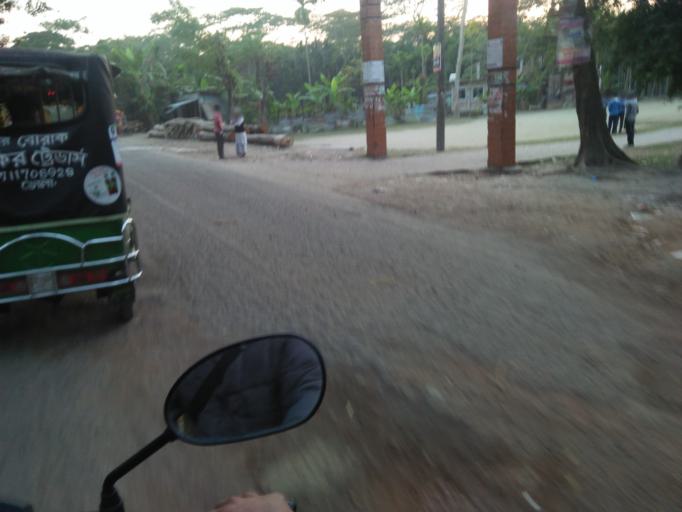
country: BD
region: Barisal
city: Bhola
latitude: 22.7576
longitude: 90.6375
